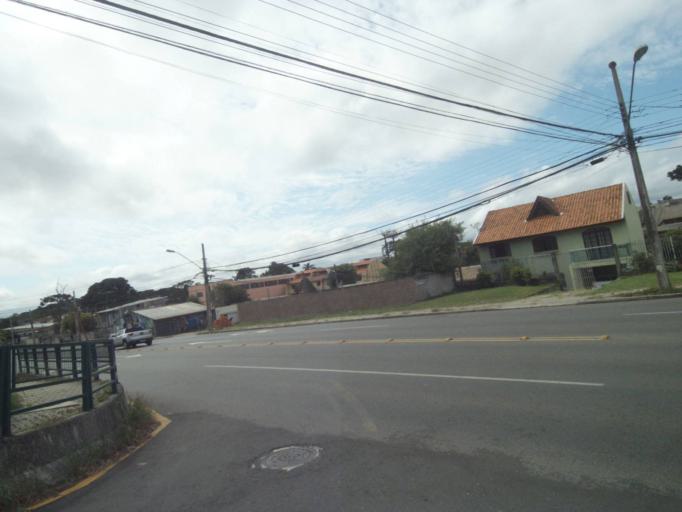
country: BR
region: Parana
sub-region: Pinhais
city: Pinhais
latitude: -25.4351
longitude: -49.2272
